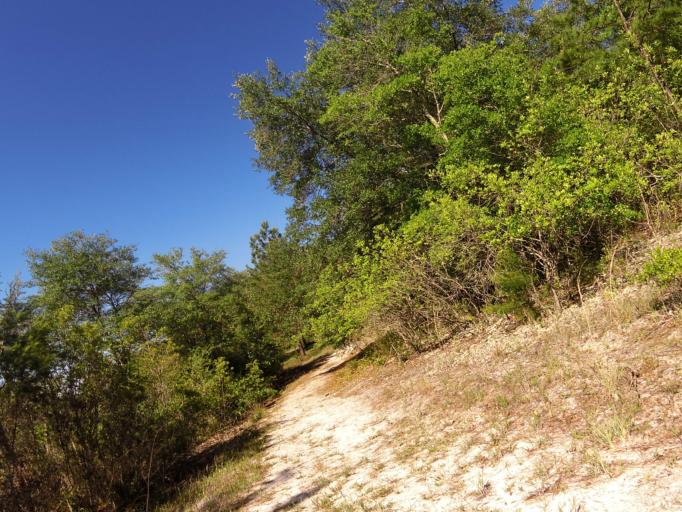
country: US
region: Florida
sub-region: Clay County
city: Keystone Heights
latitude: 29.8203
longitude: -81.9427
